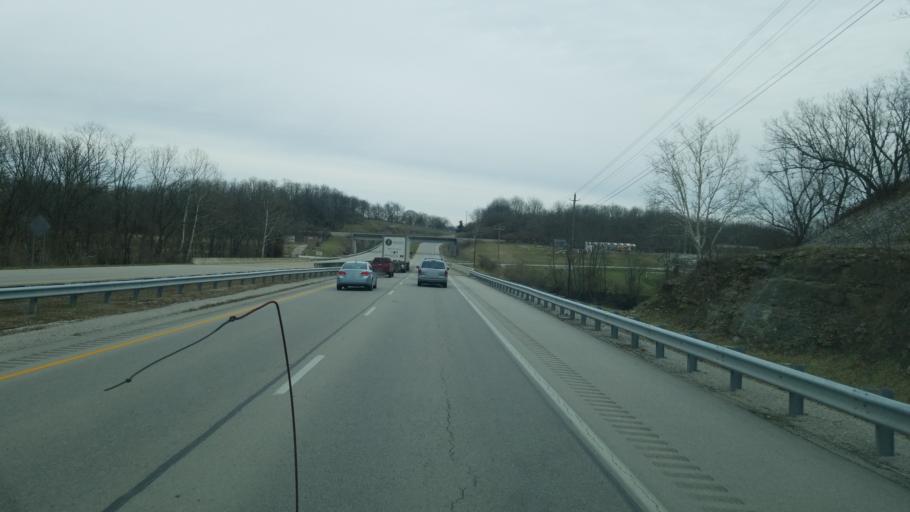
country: US
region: Kentucky
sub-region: Bourbon County
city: Paris
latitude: 38.2259
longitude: -84.2549
